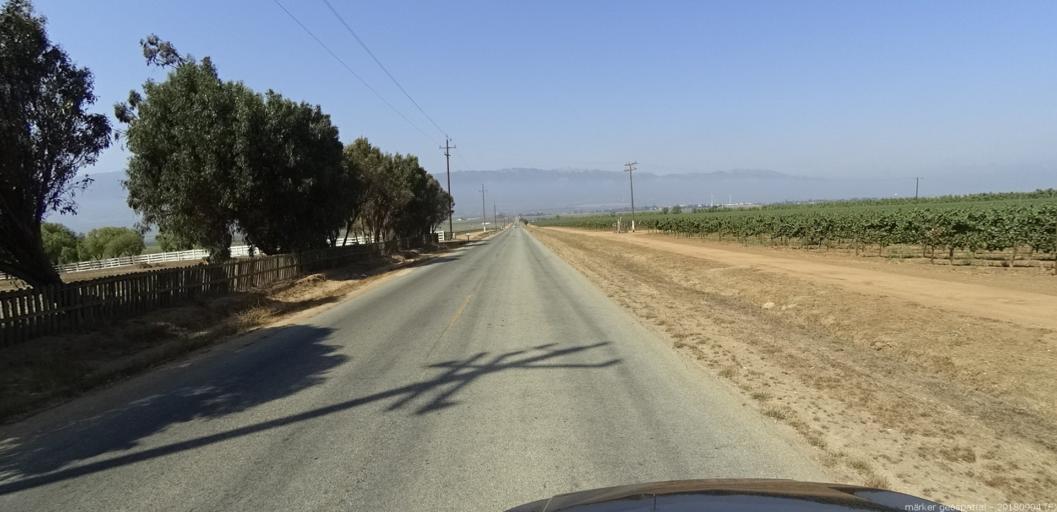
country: US
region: California
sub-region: Monterey County
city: Gonzales
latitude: 36.5004
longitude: -121.4016
